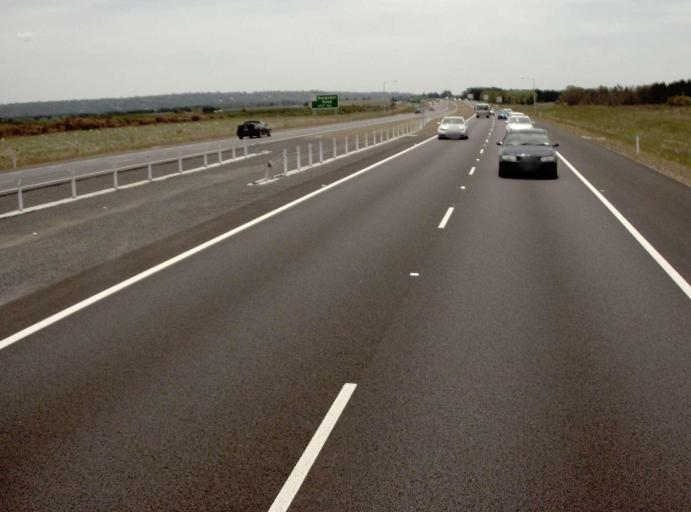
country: AU
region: Victoria
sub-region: Mornington Peninsula
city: Moorooduc
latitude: -38.2466
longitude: 145.1209
